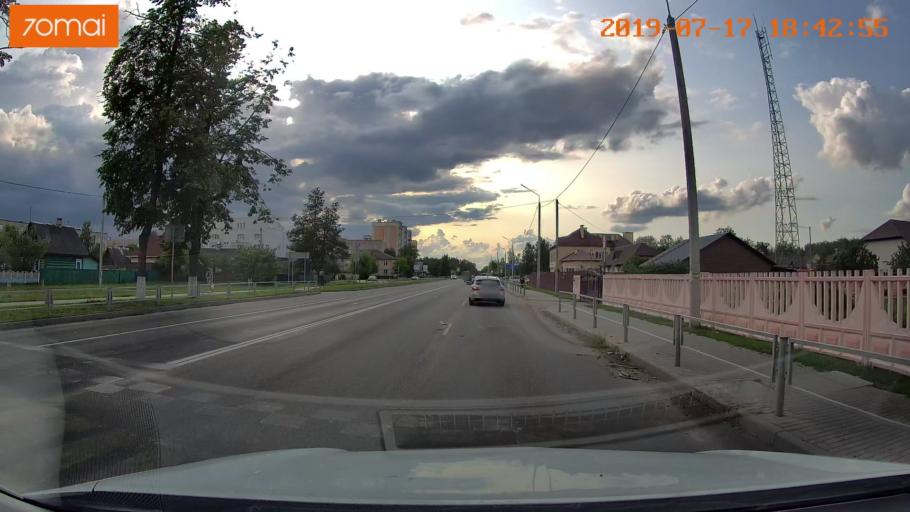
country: BY
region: Mogilev
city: Asipovichy
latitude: 53.3117
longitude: 28.6438
